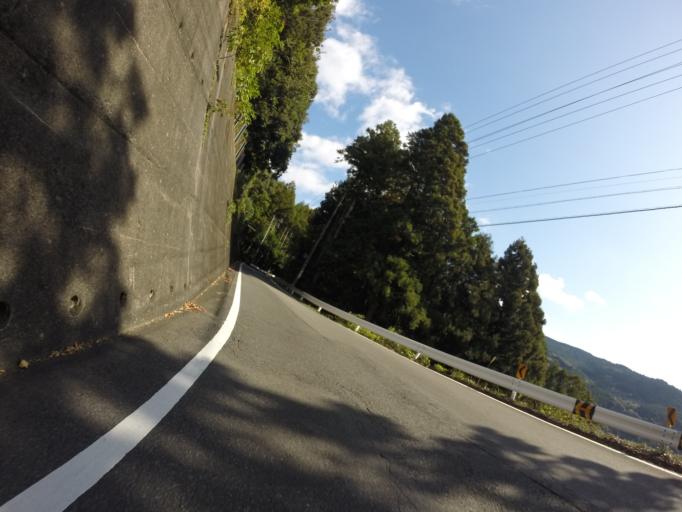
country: JP
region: Shizuoka
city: Kanaya
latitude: 34.9567
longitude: 138.0837
